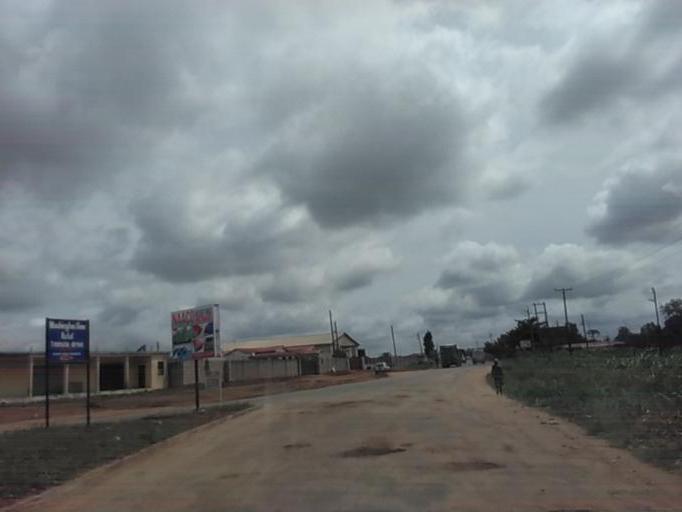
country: GH
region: Ashanti
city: Mamponteng
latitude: 6.7288
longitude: -1.4605
